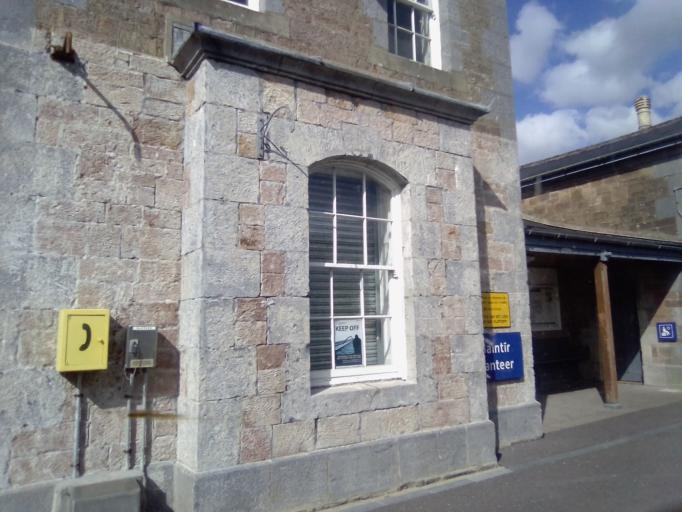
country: IE
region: Munster
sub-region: County Cork
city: Kanturk
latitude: 52.1289
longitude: -8.8991
